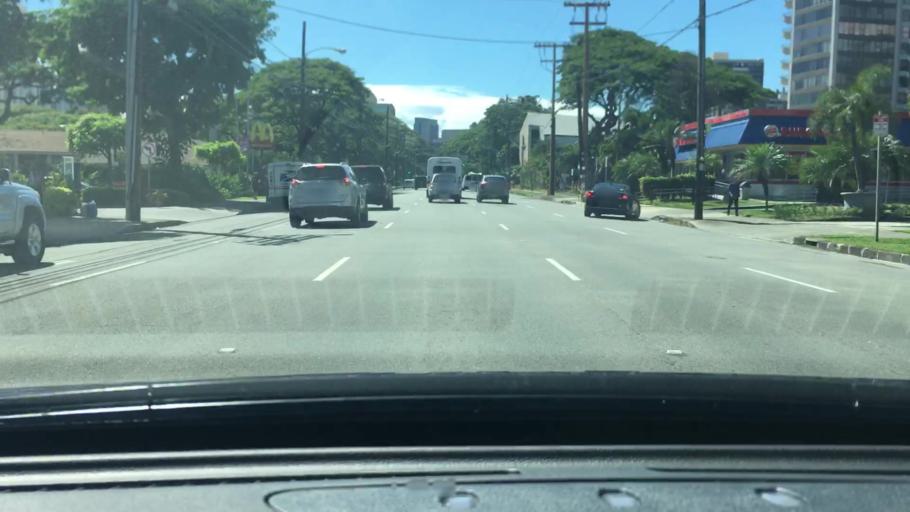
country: US
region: Hawaii
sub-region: Honolulu County
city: Honolulu
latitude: 21.3026
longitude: -157.8460
